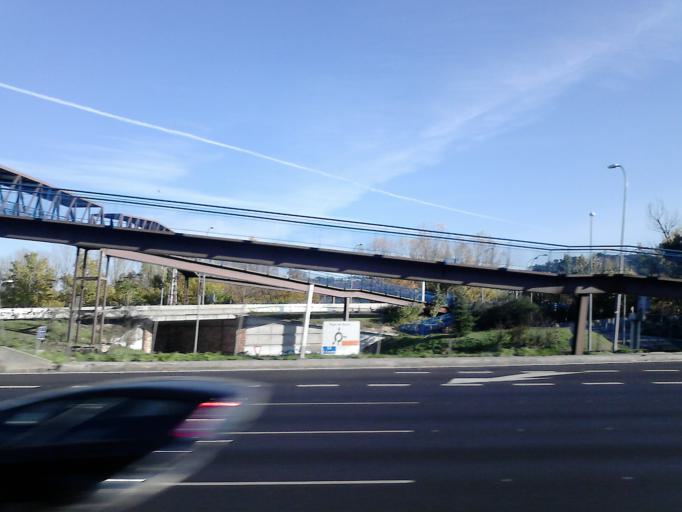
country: ES
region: Madrid
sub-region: Provincia de Madrid
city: Moncloa-Aravaca
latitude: 40.4591
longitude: -3.7489
